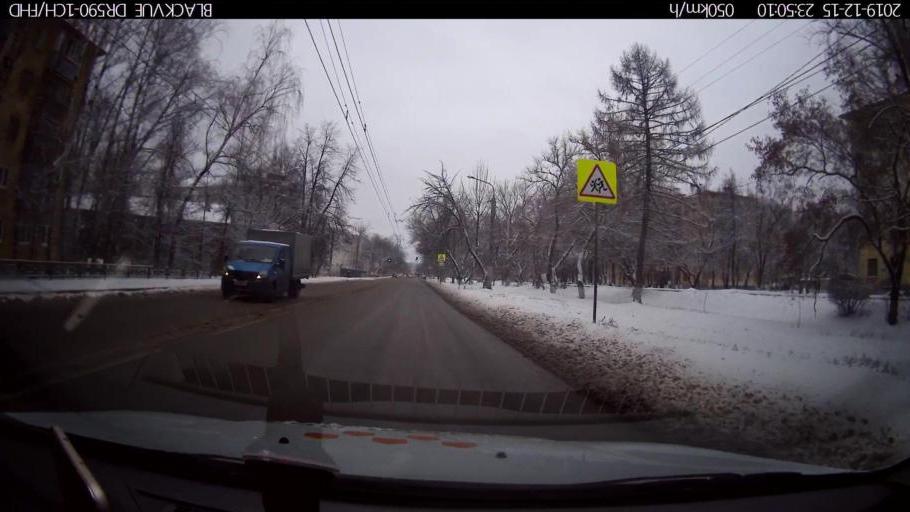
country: RU
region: Nizjnij Novgorod
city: Nizhniy Novgorod
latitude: 56.2812
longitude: 43.9314
